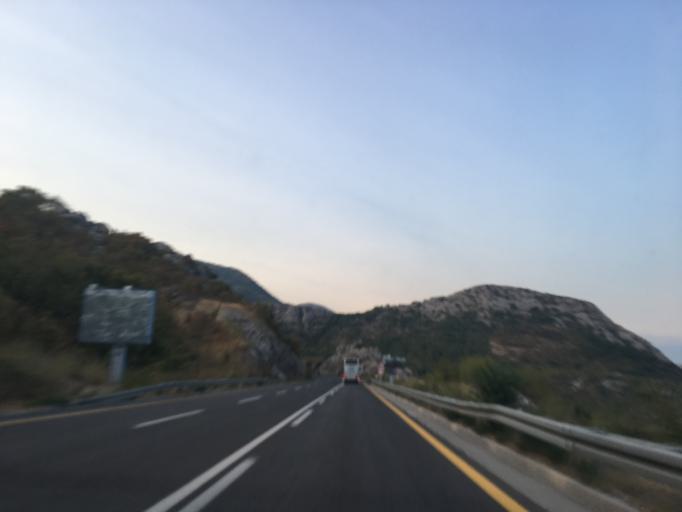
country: ME
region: Bar
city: Sutomore
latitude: 42.2170
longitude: 19.0503
